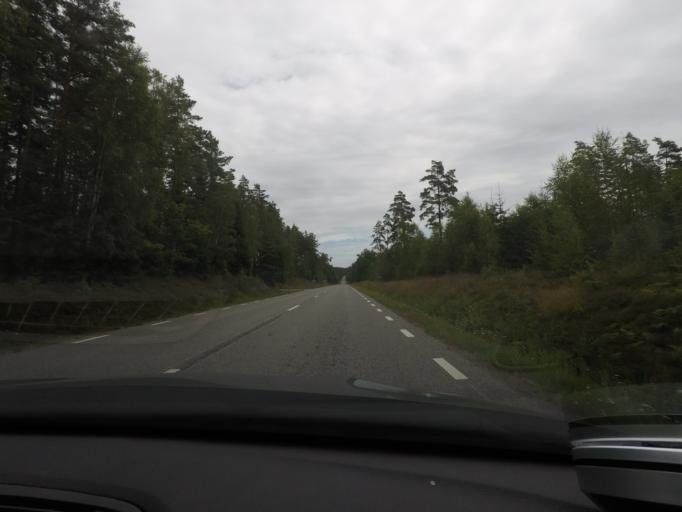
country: SE
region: Blekinge
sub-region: Olofstroms Kommun
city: Olofstroem
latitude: 56.4526
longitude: 14.5768
